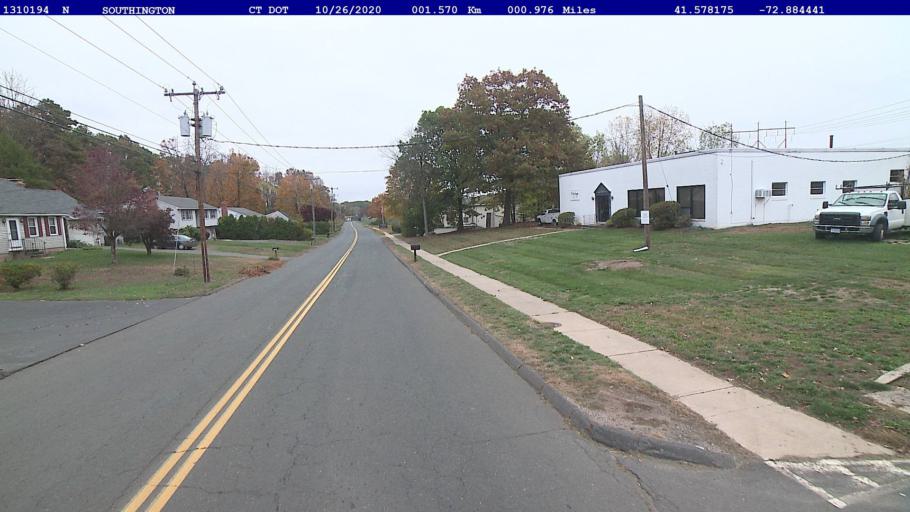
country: US
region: Connecticut
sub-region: New Haven County
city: Cheshire Village
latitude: 41.5782
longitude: -72.8844
